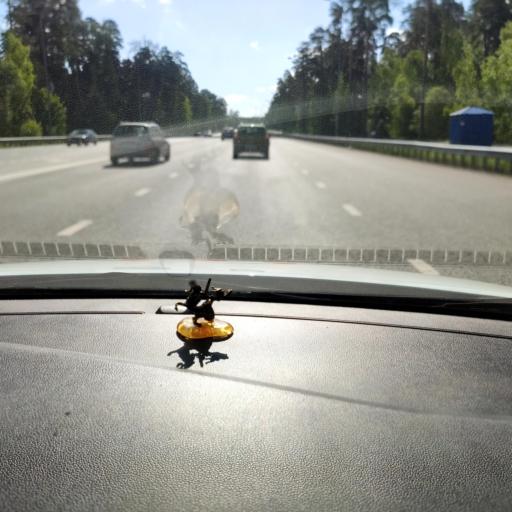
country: RU
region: Tatarstan
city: Staroye Arakchino
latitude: 55.8401
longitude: 48.9688
